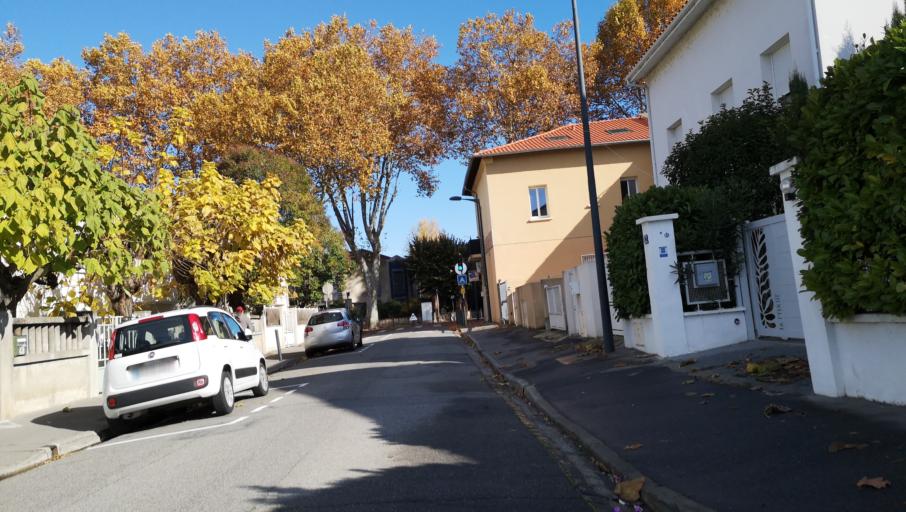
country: FR
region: Midi-Pyrenees
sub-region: Departement de la Haute-Garonne
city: Blagnac
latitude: 43.6152
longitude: 1.4094
